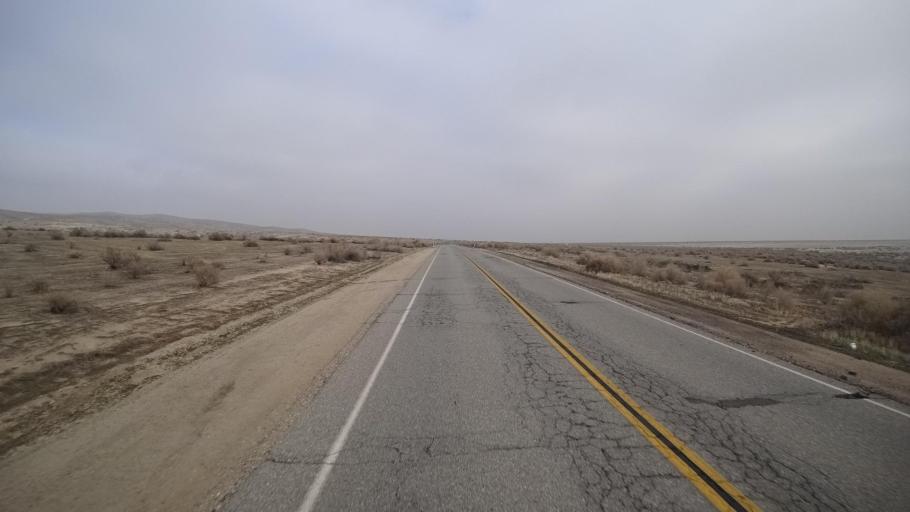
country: US
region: California
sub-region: Kern County
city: South Taft
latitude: 35.1322
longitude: -119.4005
